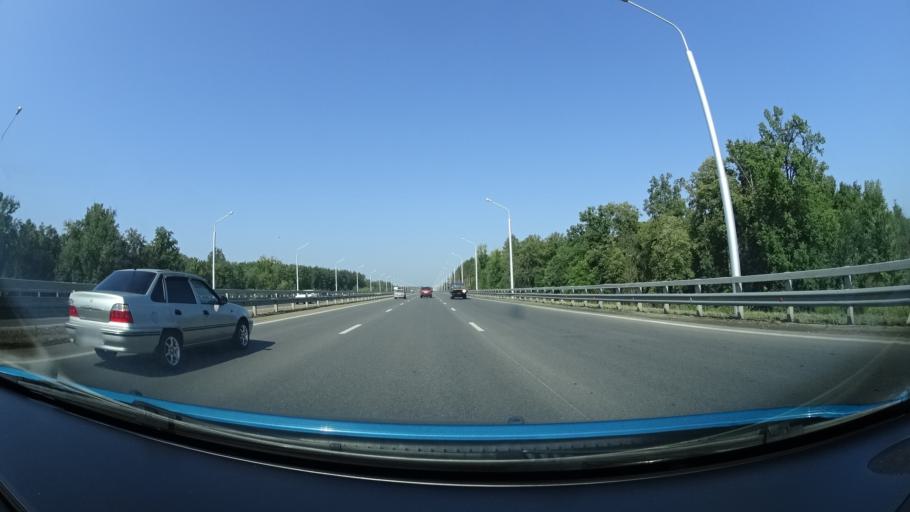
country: RU
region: Bashkortostan
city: Ufa
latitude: 54.7785
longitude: 55.9381
